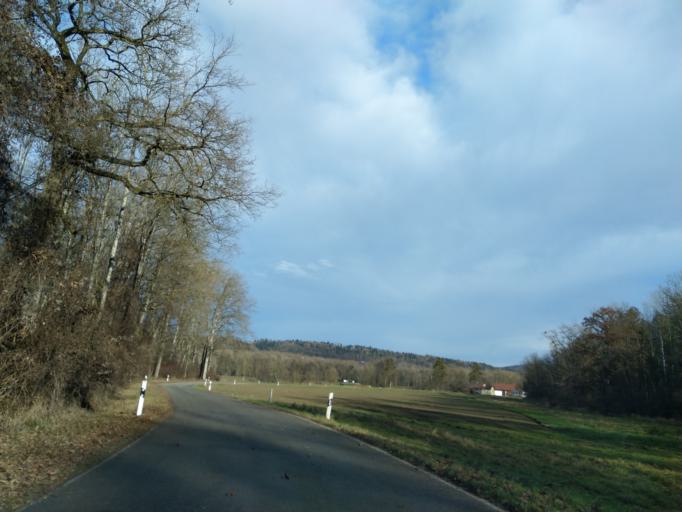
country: DE
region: Bavaria
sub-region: Lower Bavaria
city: Moos
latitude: 48.7926
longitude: 12.9737
